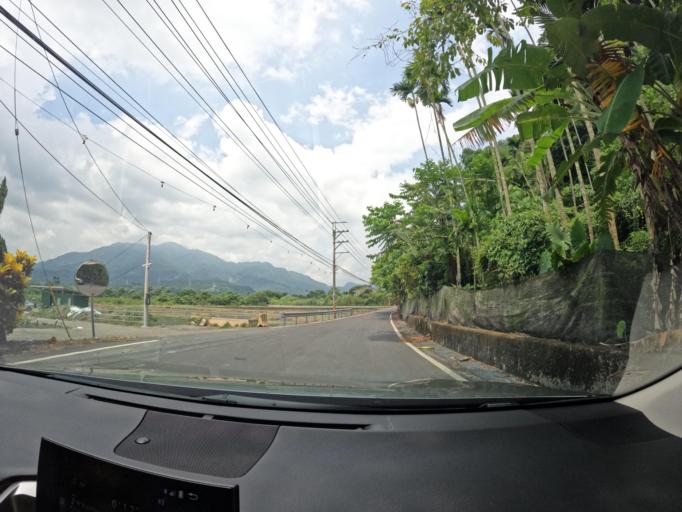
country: TW
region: Taiwan
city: Lugu
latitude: 23.8100
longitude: 120.8026
